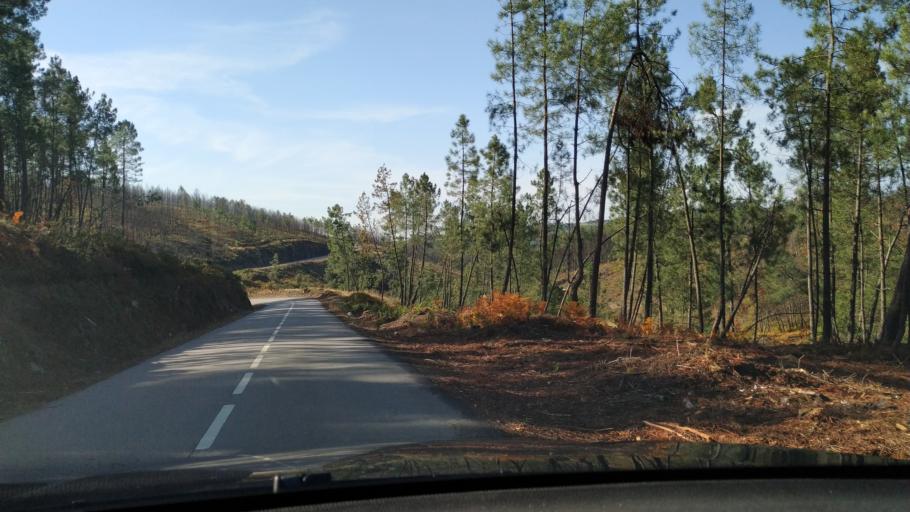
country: PT
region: Vila Real
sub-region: Sabrosa
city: Vilela
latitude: 41.2401
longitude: -7.6379
